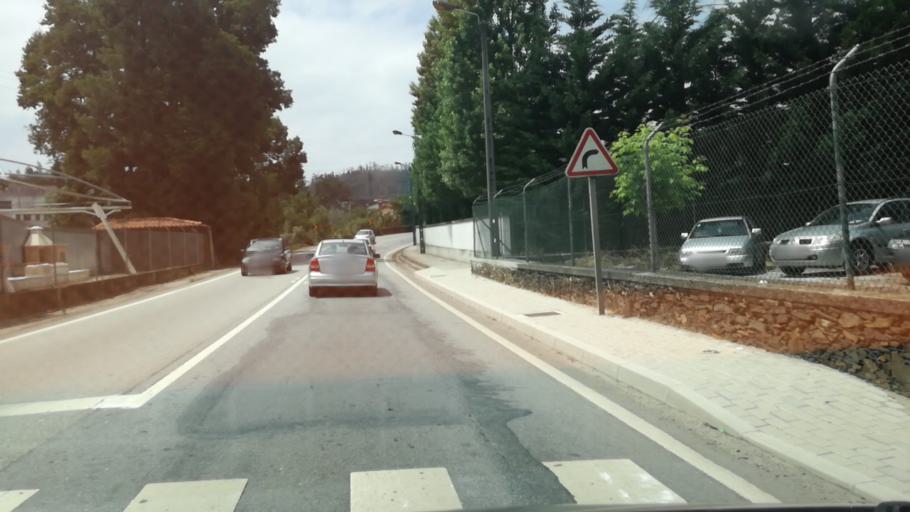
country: PT
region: Porto
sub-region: Trofa
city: Sao Romao do Coronado
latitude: 41.3163
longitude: -8.5772
